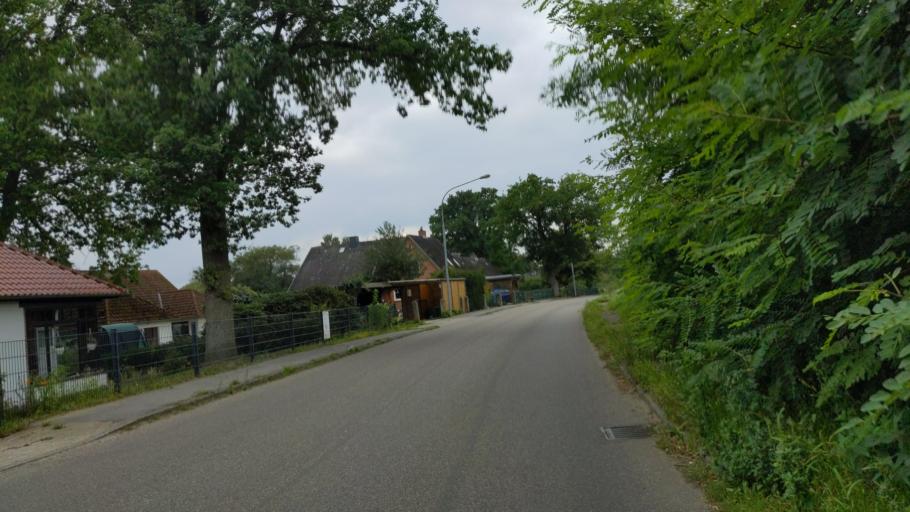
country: DE
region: Schleswig-Holstein
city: Klempau
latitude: 53.7876
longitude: 10.6813
